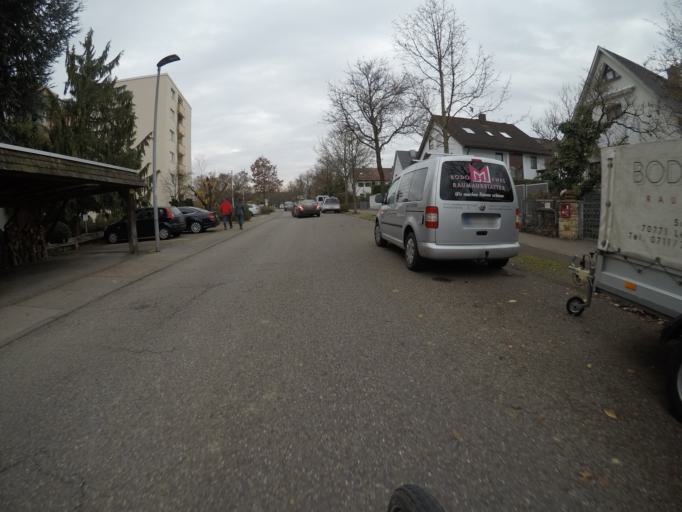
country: DE
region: Baden-Wuerttemberg
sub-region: Regierungsbezirk Stuttgart
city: Leinfelden-Echterdingen
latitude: 48.6917
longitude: 9.1384
